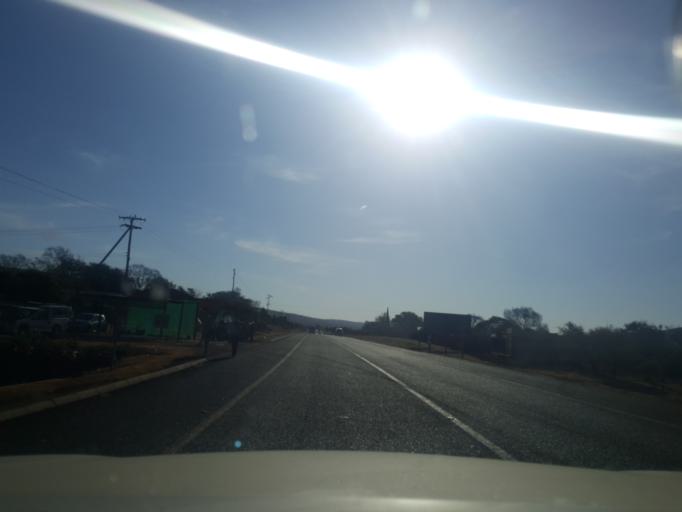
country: ZA
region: North-West
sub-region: Ngaka Modiri Molema District Municipality
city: Zeerust
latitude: -25.4468
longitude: 25.8628
